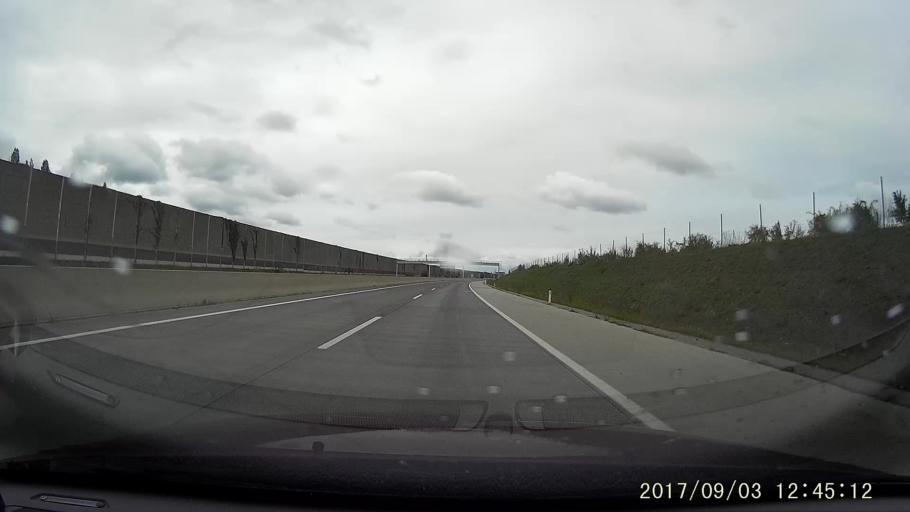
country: AT
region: Lower Austria
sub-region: Politischer Bezirk Korneuburg
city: Korneuburg
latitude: 48.3623
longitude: 16.3370
